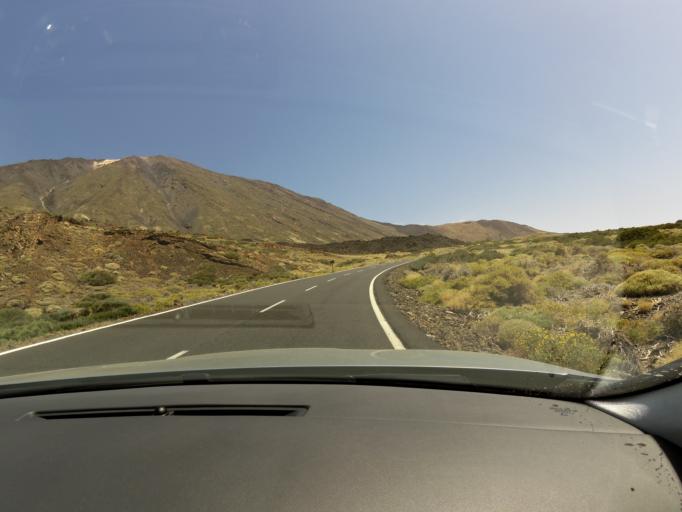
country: ES
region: Canary Islands
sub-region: Provincia de Santa Cruz de Tenerife
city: Vilaflor
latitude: 28.2434
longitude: -16.6303
